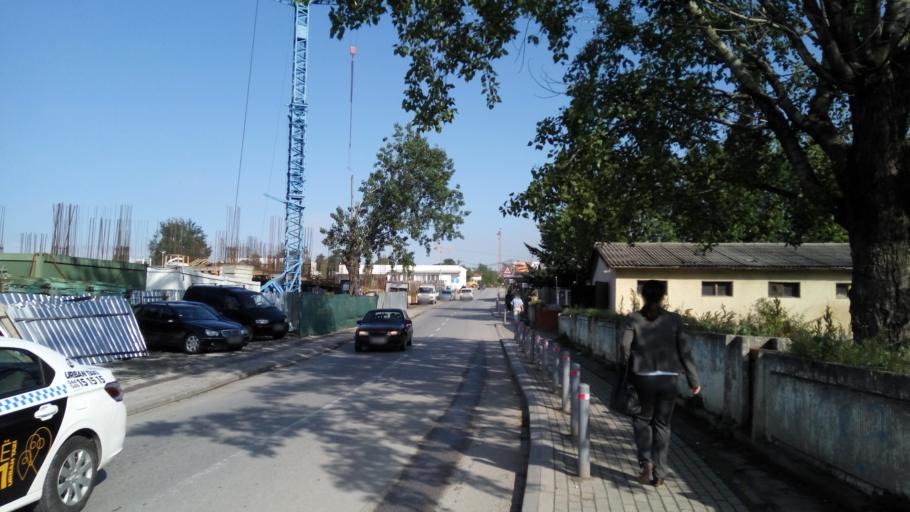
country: XK
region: Pristina
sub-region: Komuna e Prishtines
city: Pristina
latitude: 42.6533
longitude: 21.1483
